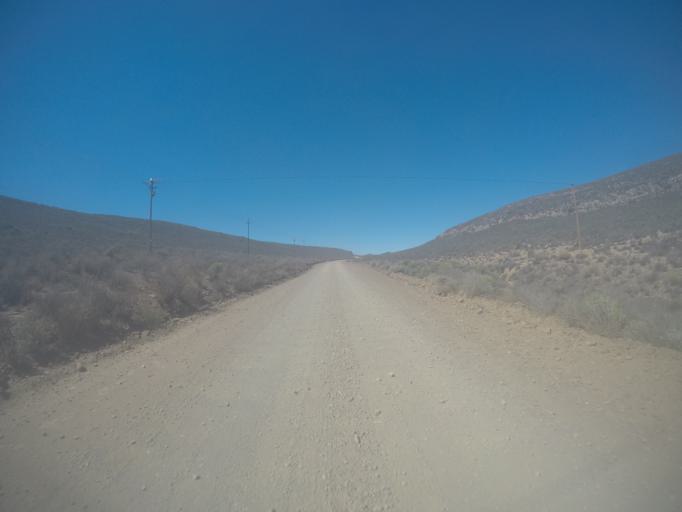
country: ZA
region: Western Cape
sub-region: West Coast District Municipality
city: Clanwilliam
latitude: -32.5248
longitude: 19.3518
